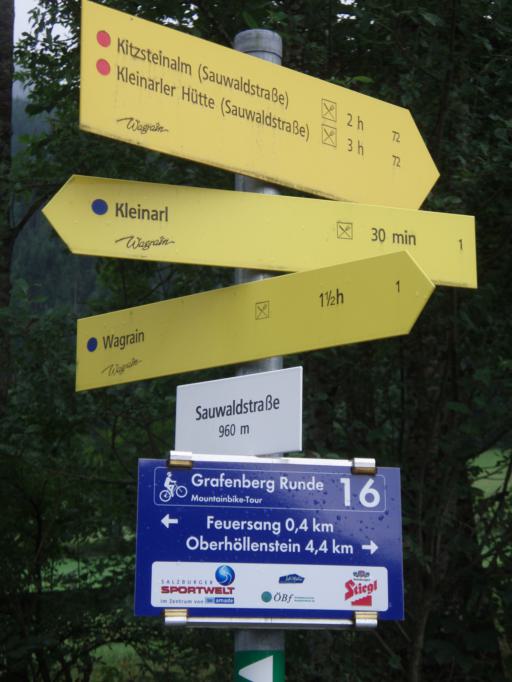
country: AT
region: Salzburg
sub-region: Politischer Bezirk Sankt Johann im Pongau
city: Kleinarl
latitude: 47.3015
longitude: 13.3031
